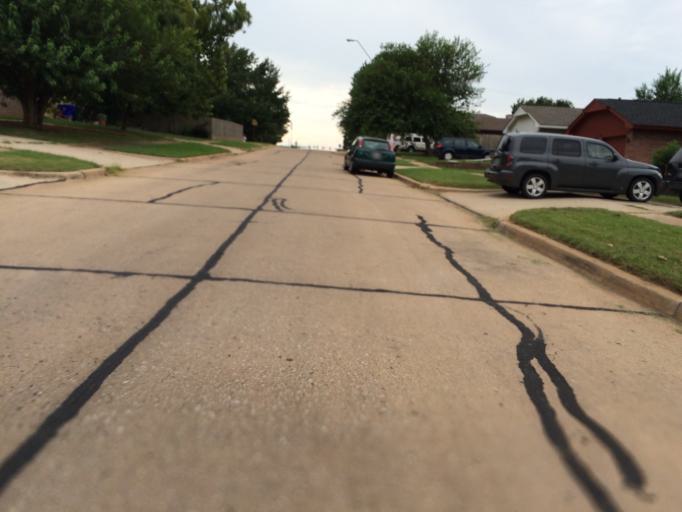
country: US
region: Oklahoma
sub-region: Cleveland County
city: Hall Park
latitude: 35.2541
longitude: -97.4206
